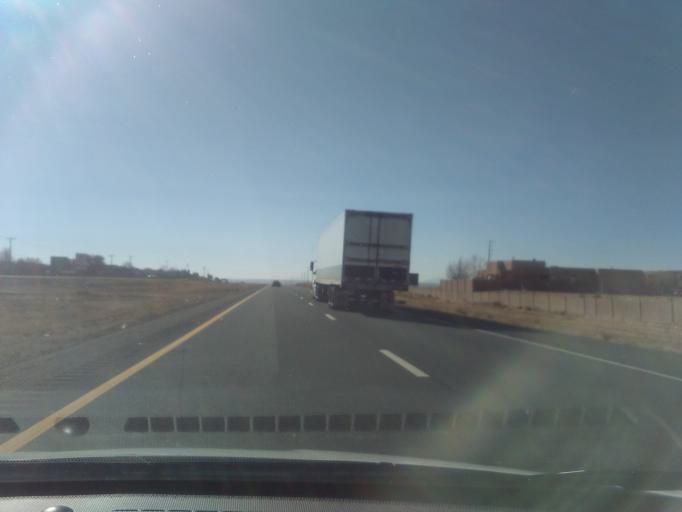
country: US
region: New Mexico
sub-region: Valencia County
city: Los Lunas
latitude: 34.8050
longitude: -106.7654
